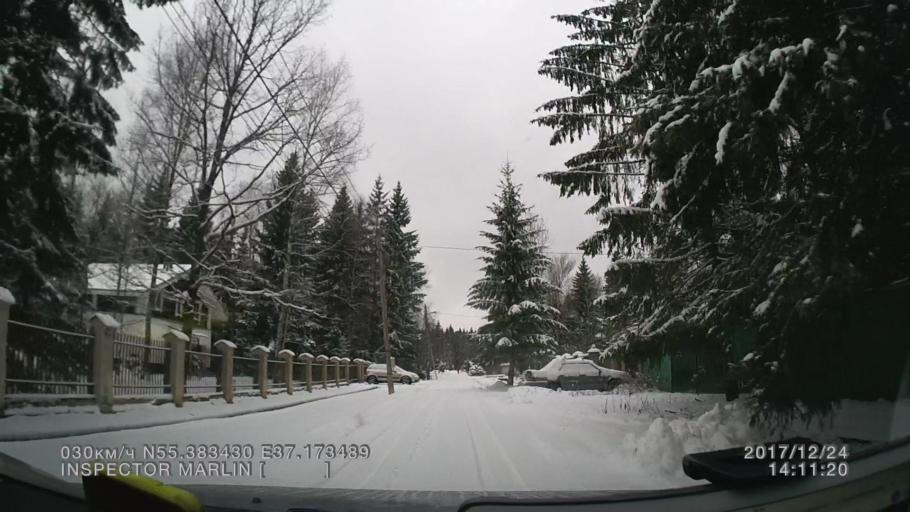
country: RU
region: Moskovskaya
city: Troitsk
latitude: 55.3835
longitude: 37.1734
